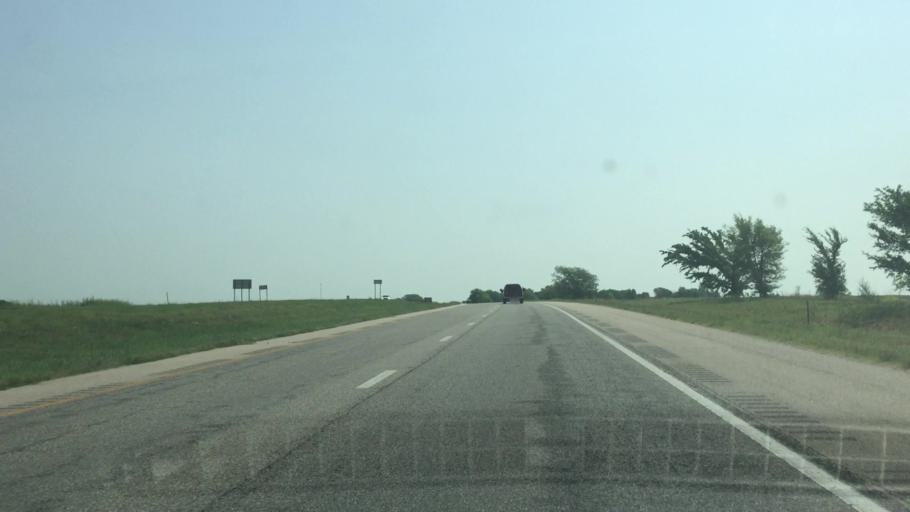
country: US
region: Kansas
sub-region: Osage County
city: Lyndon
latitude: 38.4259
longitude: -95.7445
